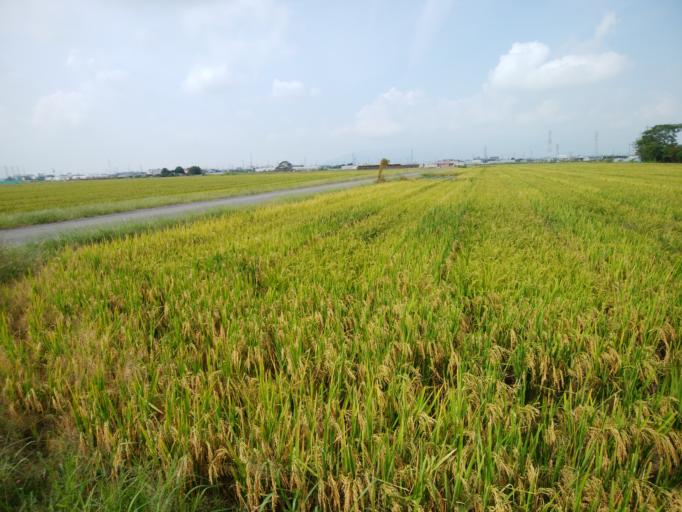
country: JP
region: Aichi
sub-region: Aisai-shi
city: Aisai
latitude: 35.1571
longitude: 136.7440
